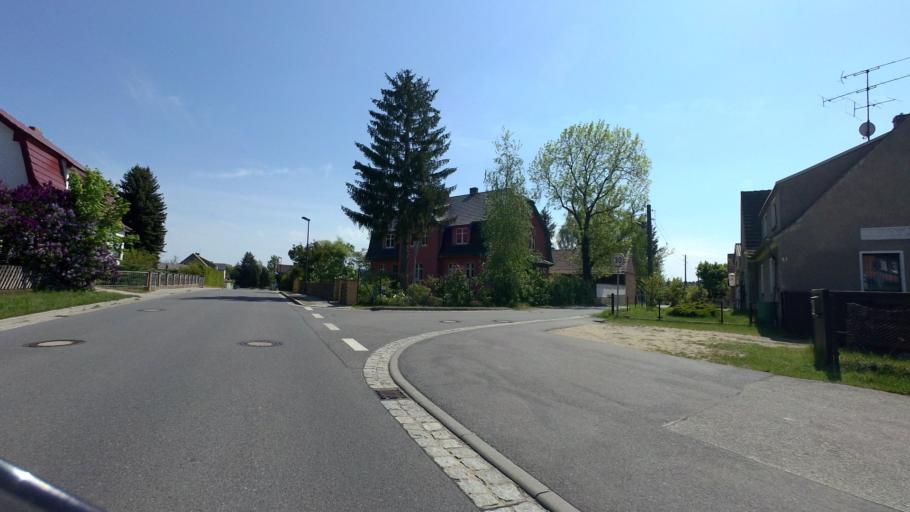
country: DE
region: Brandenburg
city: Neu Zauche
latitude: 52.0399
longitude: 14.0341
